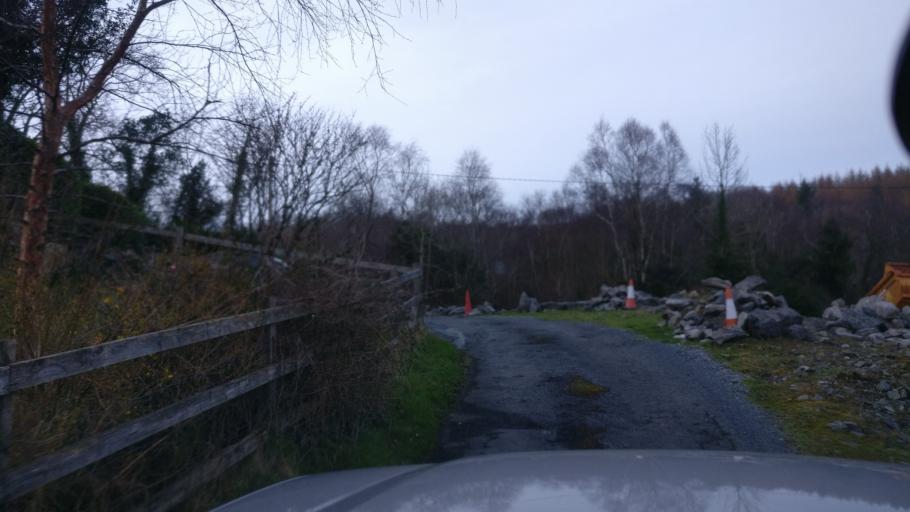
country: IE
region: Connaught
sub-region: County Galway
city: Oughterard
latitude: 53.5189
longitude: -9.4397
